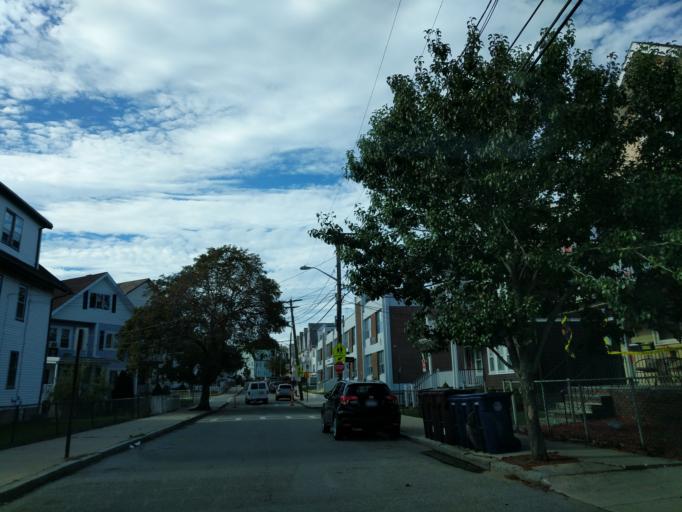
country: US
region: Massachusetts
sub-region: Middlesex County
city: Everett
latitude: 42.4118
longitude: -71.0387
